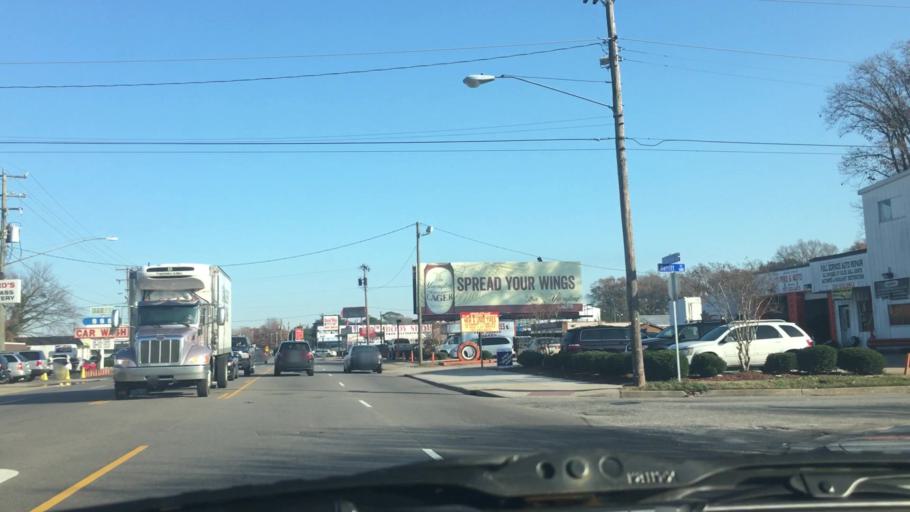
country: US
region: Virginia
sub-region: City of Norfolk
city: Norfolk
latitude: 36.9149
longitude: -76.2462
